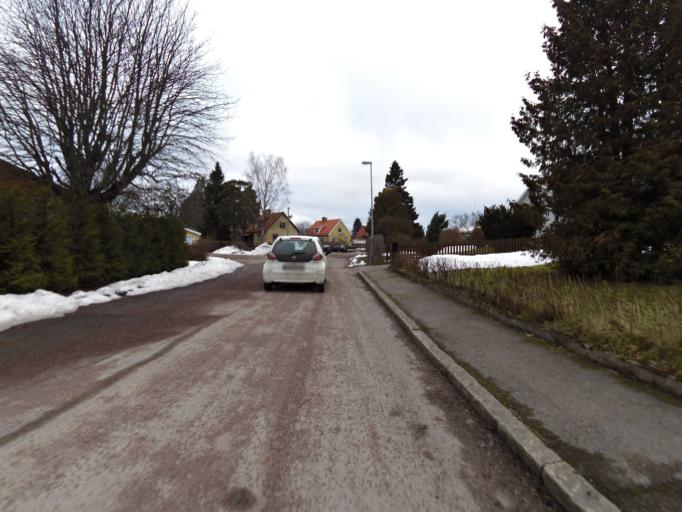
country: SE
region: Gaevleborg
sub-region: Gavle Kommun
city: Gavle
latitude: 60.6614
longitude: 17.1220
